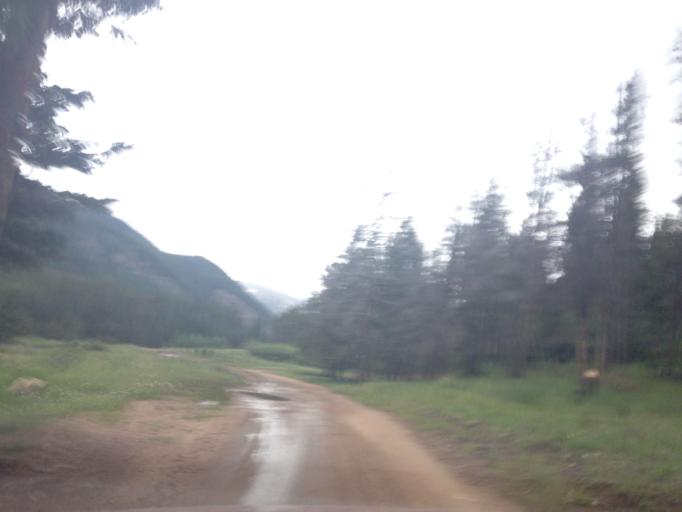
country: US
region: Colorado
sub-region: Clear Creek County
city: Georgetown
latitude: 39.5471
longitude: -105.7486
